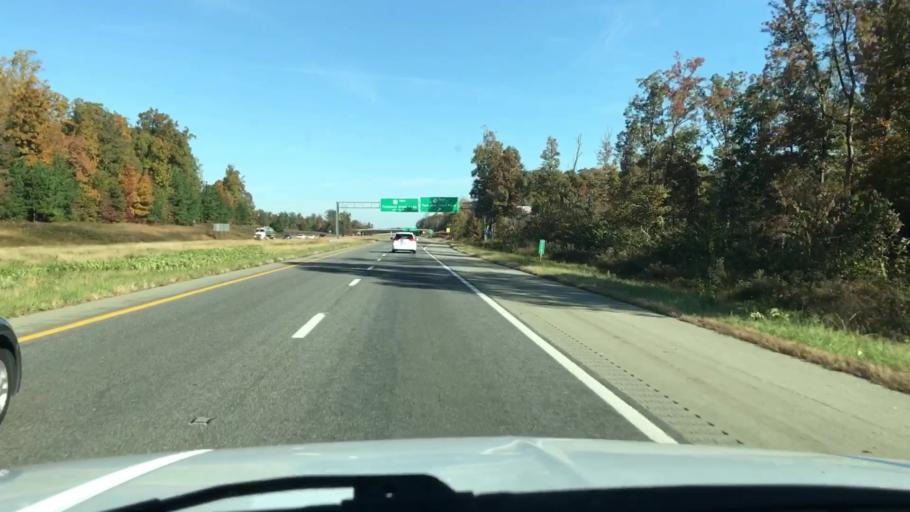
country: US
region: Virginia
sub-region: Henrico County
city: Short Pump
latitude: 37.6239
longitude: -77.6633
